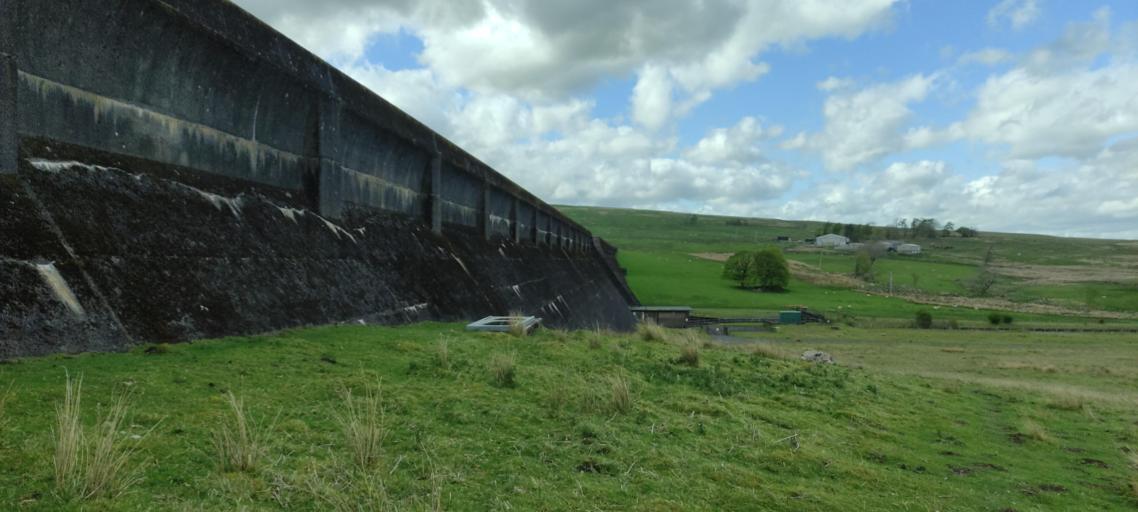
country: GB
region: England
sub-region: Cumbria
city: Kendal
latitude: 54.4966
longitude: -2.6906
